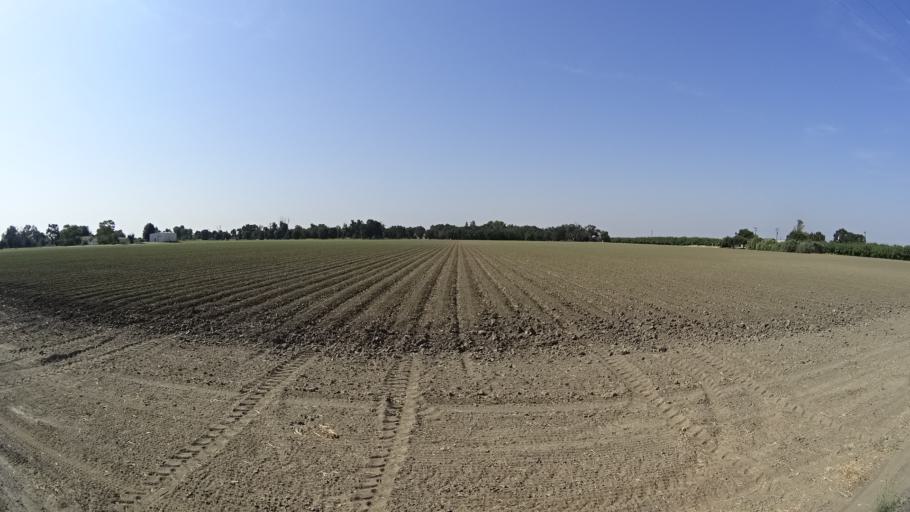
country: US
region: California
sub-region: Kings County
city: Lemoore
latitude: 36.3369
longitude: -119.8542
